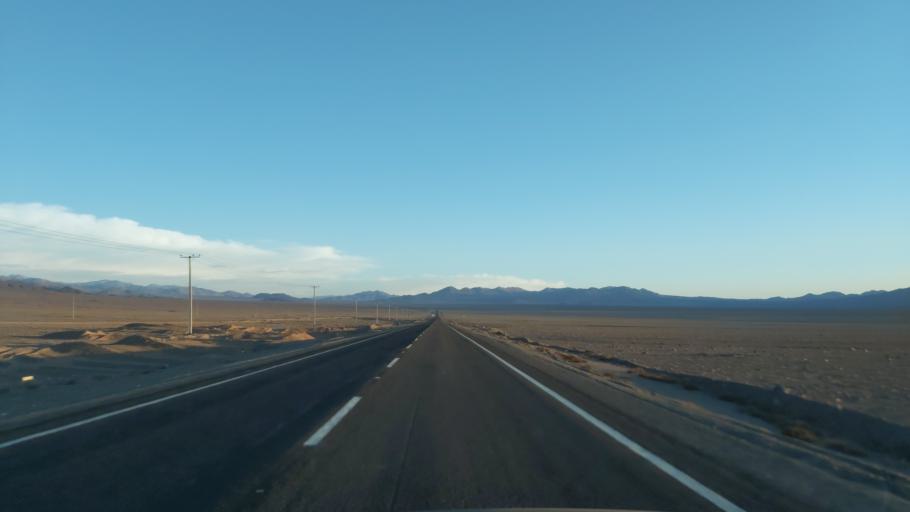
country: CL
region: Atacama
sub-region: Provincia de Chanaral
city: Diego de Almagro
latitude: -26.6156
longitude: -69.9528
